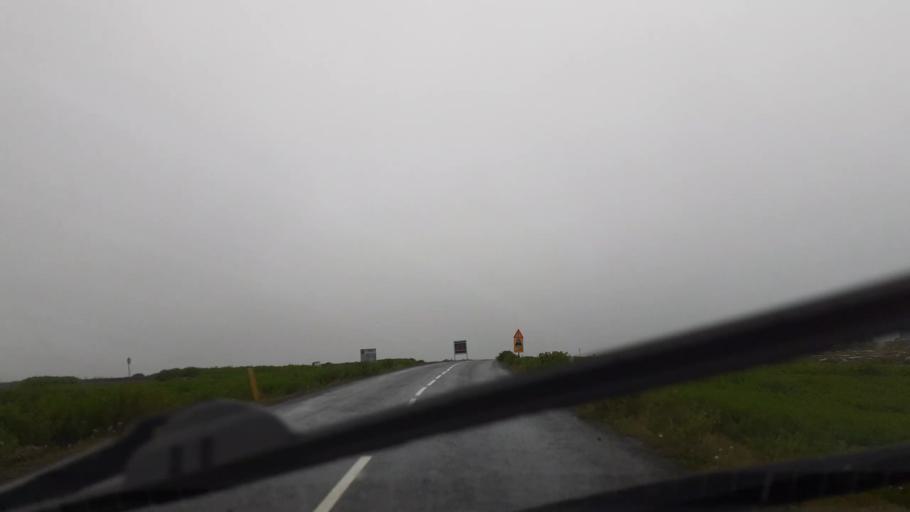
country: IS
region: Northeast
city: Husavik
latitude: 66.4604
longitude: -15.9517
